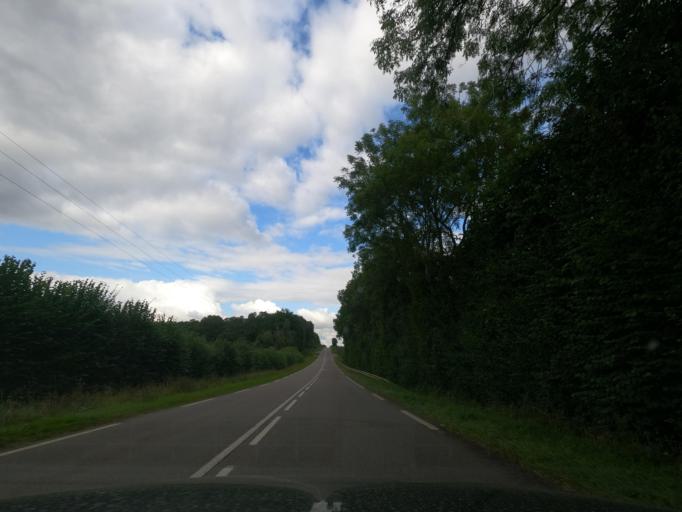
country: FR
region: Lower Normandy
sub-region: Departement de l'Orne
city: Gace
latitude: 48.8826
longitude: 0.3900
